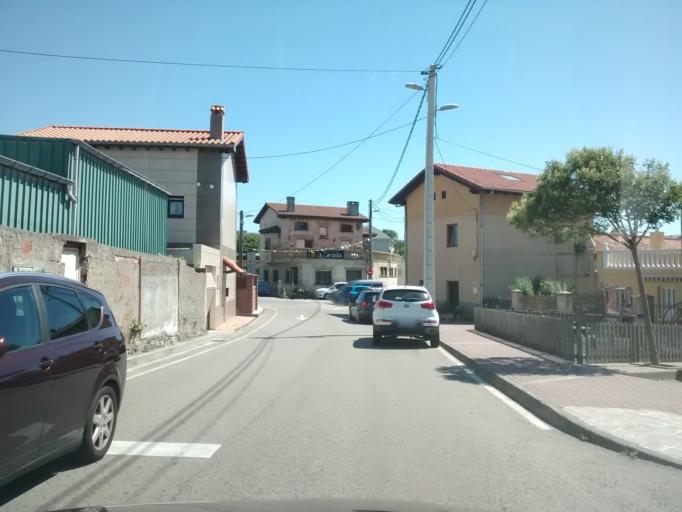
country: ES
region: Cantabria
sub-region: Provincia de Cantabria
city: Santander
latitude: 43.4712
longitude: -3.8306
